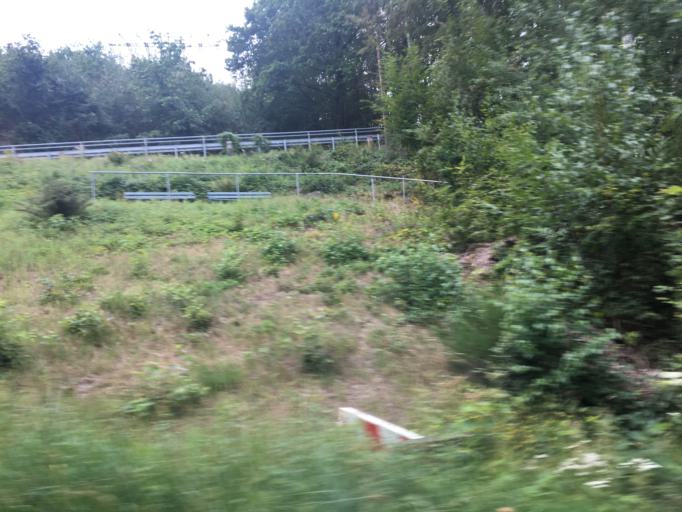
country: DE
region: Saxony
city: Coswig
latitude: 51.0887
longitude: 13.6043
